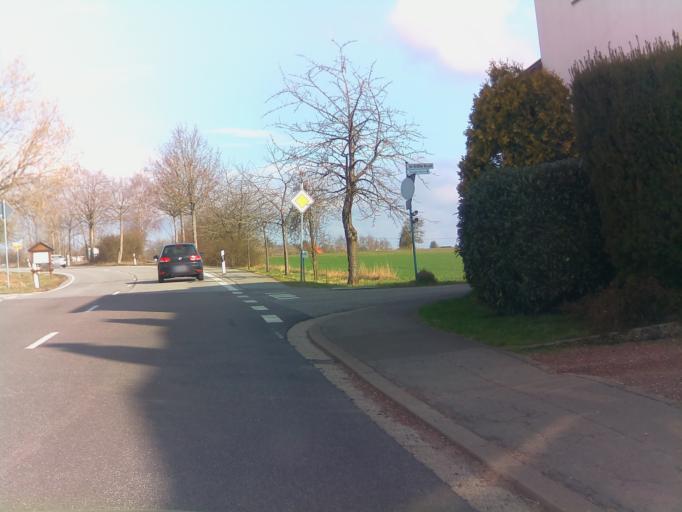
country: DE
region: Saarland
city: Gersheim
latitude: 49.2199
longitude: 7.1856
